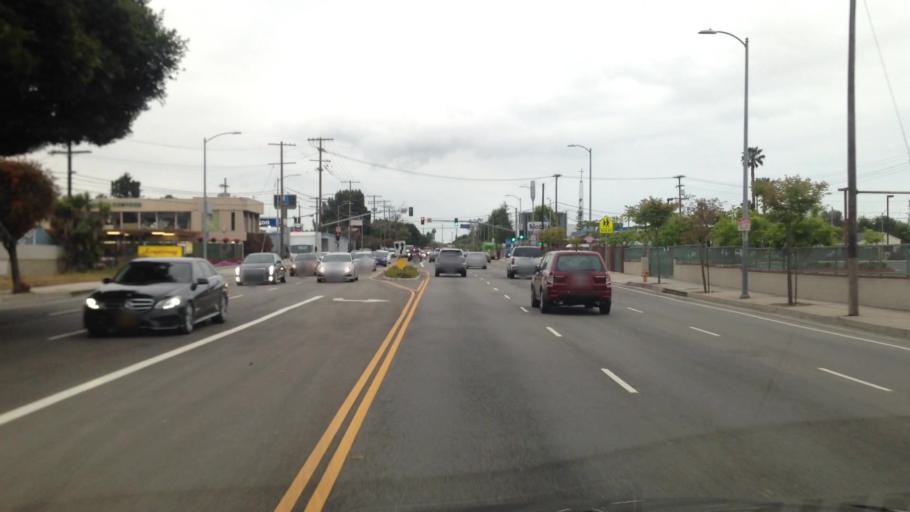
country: US
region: California
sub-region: Los Angeles County
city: Ladera Heights
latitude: 33.9731
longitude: -118.3946
